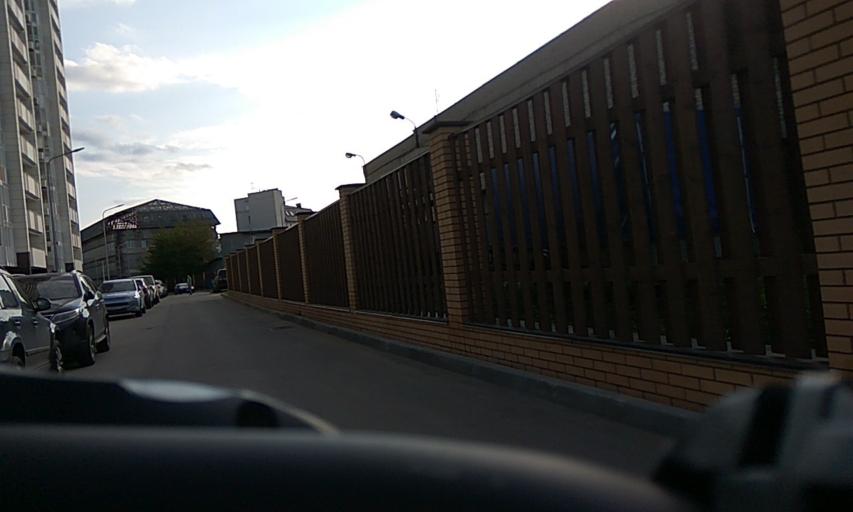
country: RU
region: Moscow
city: Kolomenskoye
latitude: 55.6817
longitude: 37.6948
